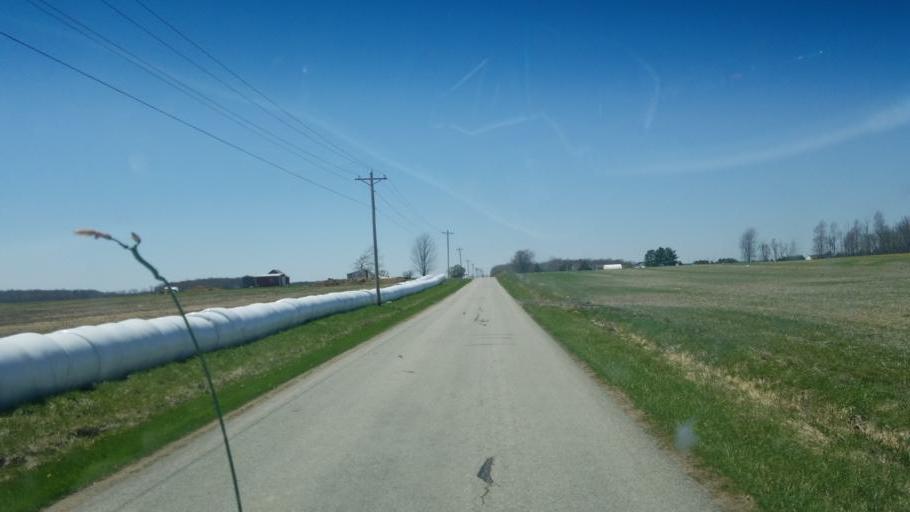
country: US
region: Ohio
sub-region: Huron County
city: Greenwich
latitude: 41.0935
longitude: -82.5030
